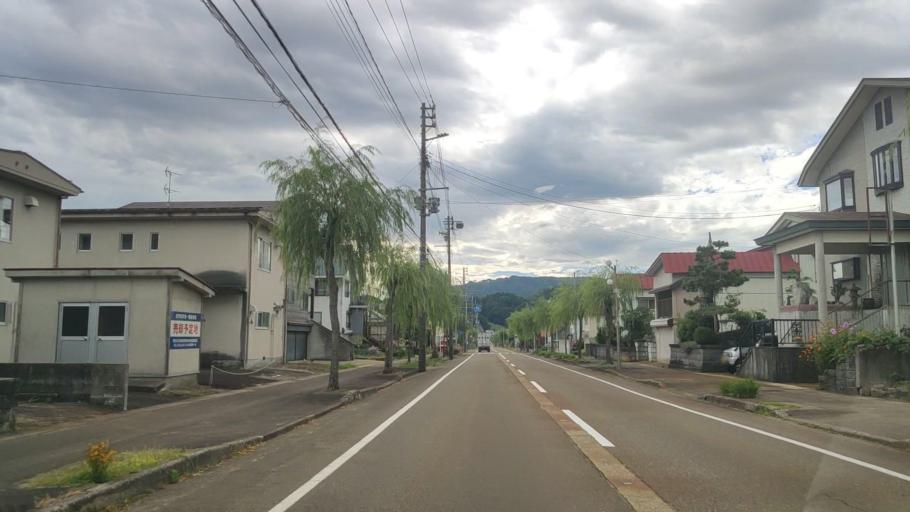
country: JP
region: Niigata
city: Arai
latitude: 37.0188
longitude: 138.2477
